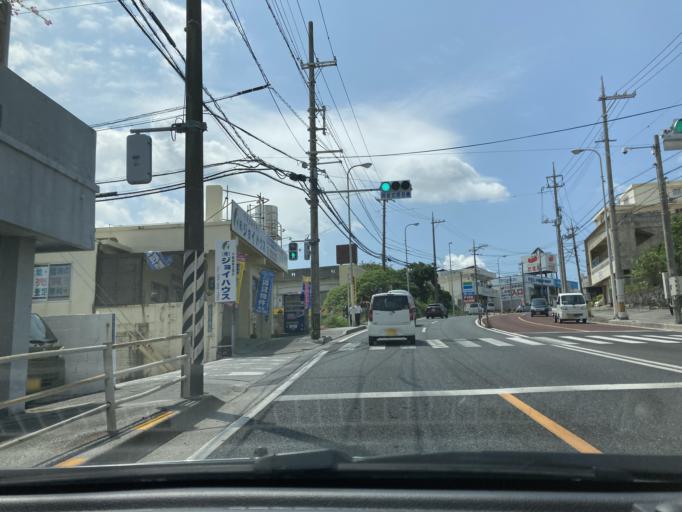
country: JP
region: Okinawa
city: Ginowan
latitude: 26.2585
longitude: 127.7579
